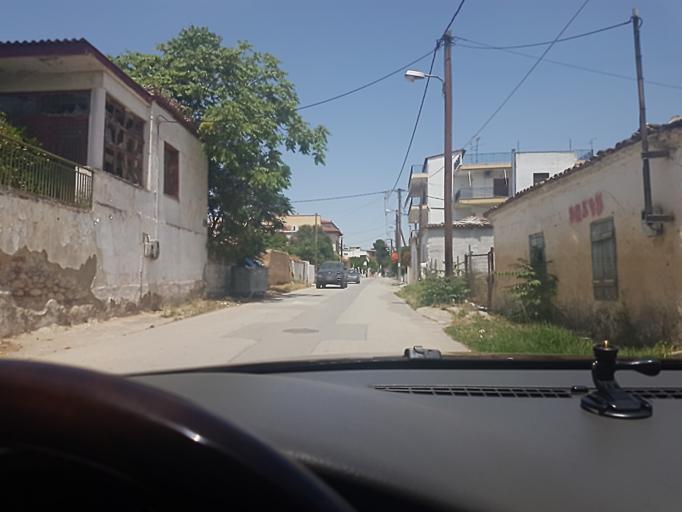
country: GR
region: Central Greece
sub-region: Nomos Evvoias
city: Vasilikon
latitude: 38.4230
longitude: 23.6681
